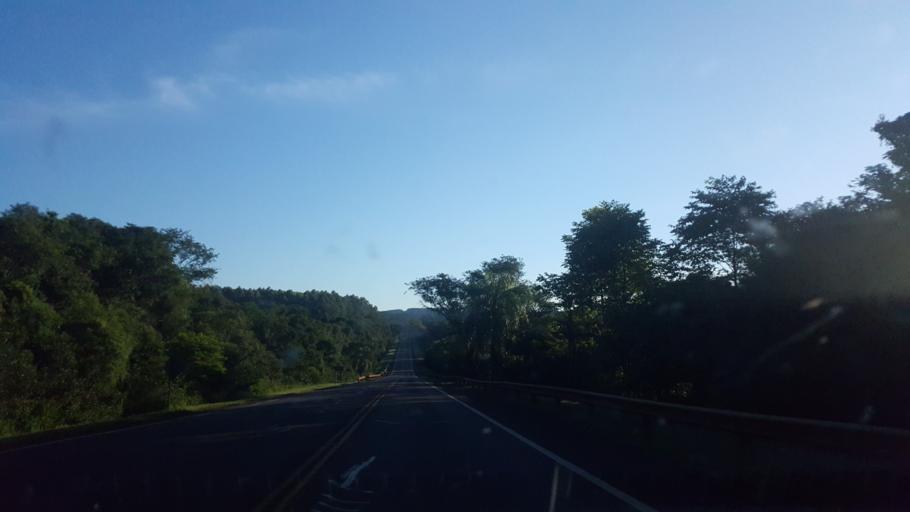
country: AR
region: Misiones
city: El Alcazar
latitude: -26.6990
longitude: -54.8369
